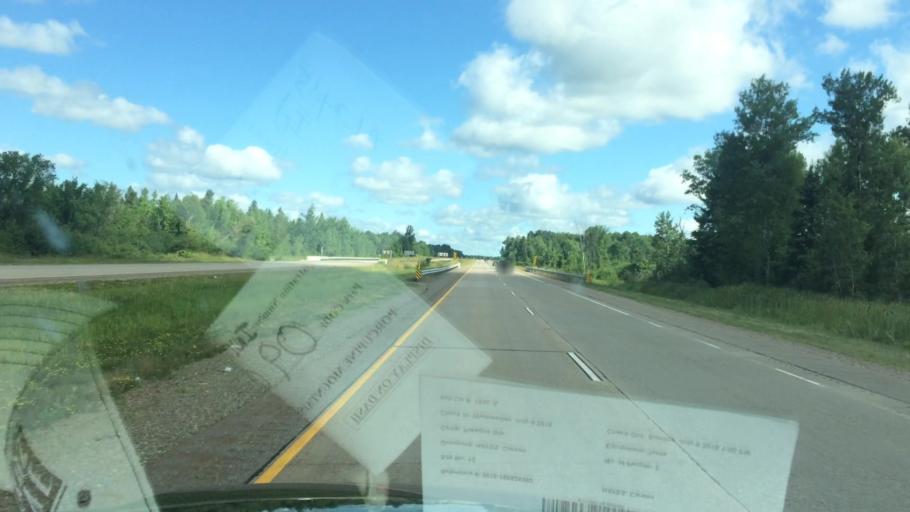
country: US
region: Wisconsin
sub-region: Lincoln County
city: Tomahawk
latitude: 45.3922
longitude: -89.6722
